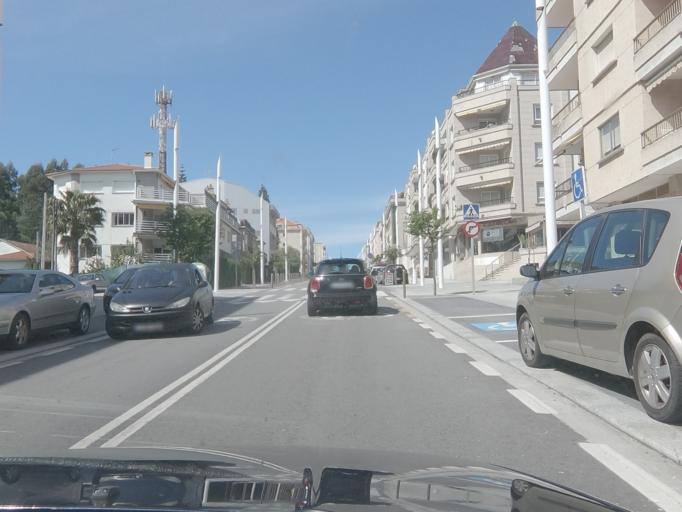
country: ES
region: Galicia
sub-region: Provincia de Pontevedra
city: Sanxenxo
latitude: 42.4027
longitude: -8.8128
